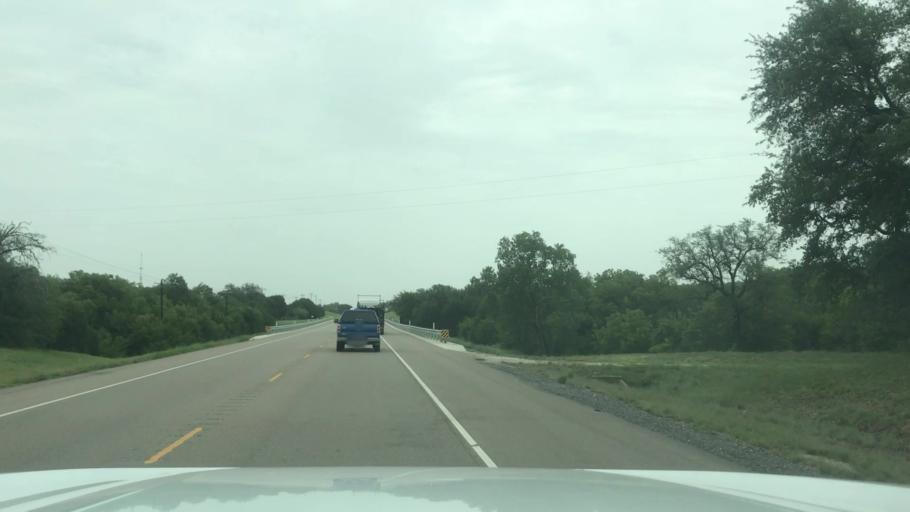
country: US
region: Texas
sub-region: Bosque County
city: Meridian
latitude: 31.9249
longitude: -97.6824
